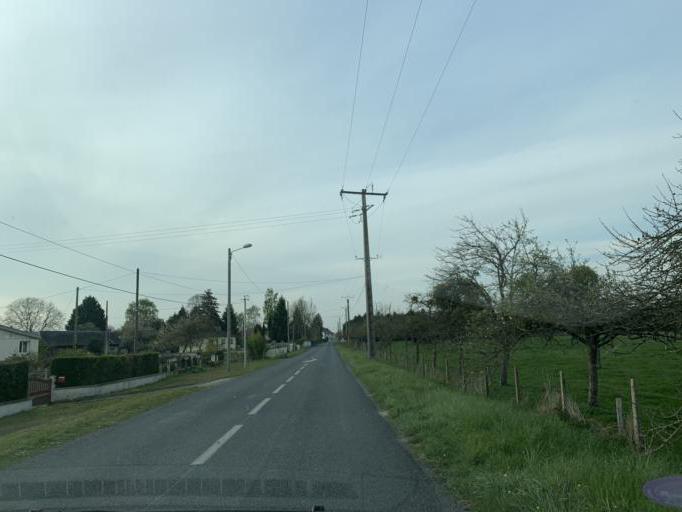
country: FR
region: Haute-Normandie
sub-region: Departement de la Seine-Maritime
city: La Mailleraye-sur-Seine
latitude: 49.4637
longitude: 0.7804
